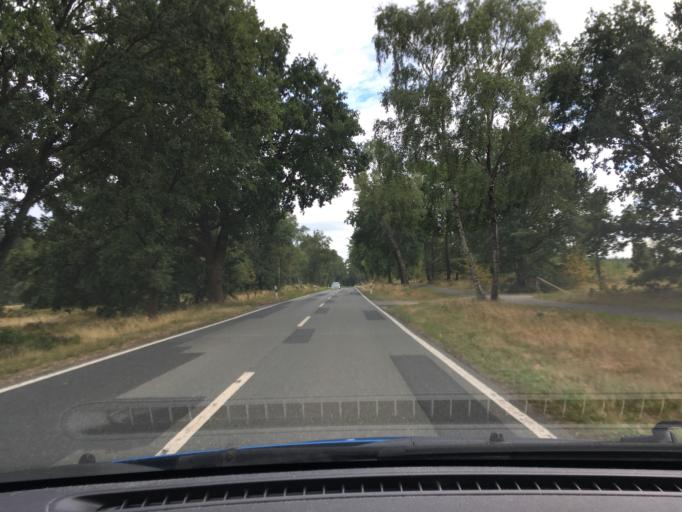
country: DE
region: Lower Saxony
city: Undeloh
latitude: 53.2143
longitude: 9.9487
